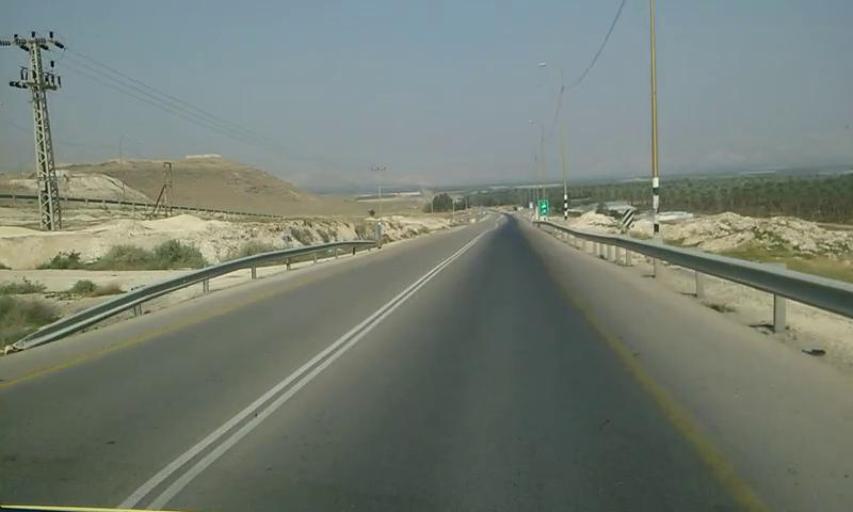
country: PS
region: West Bank
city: Al `Awja
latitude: 31.9725
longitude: 35.4700
